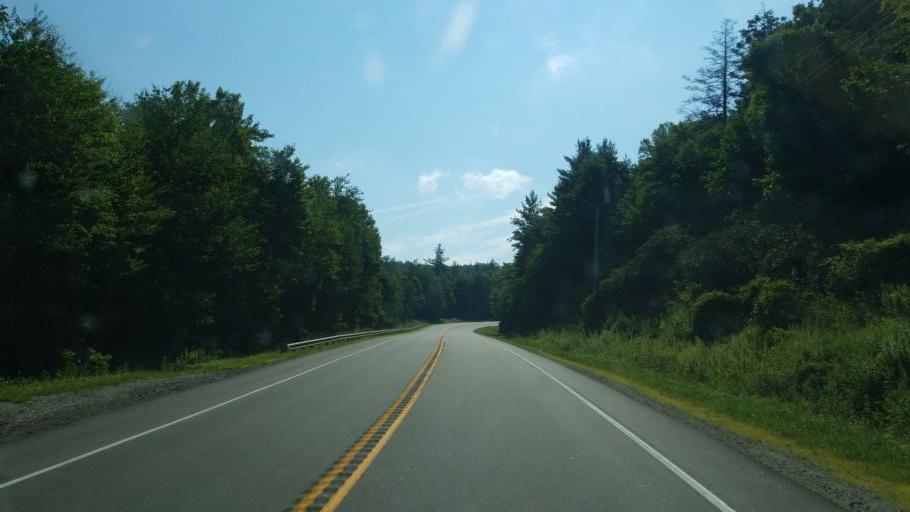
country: US
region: North Carolina
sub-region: Avery County
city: Newland
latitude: 35.9776
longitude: -81.8963
